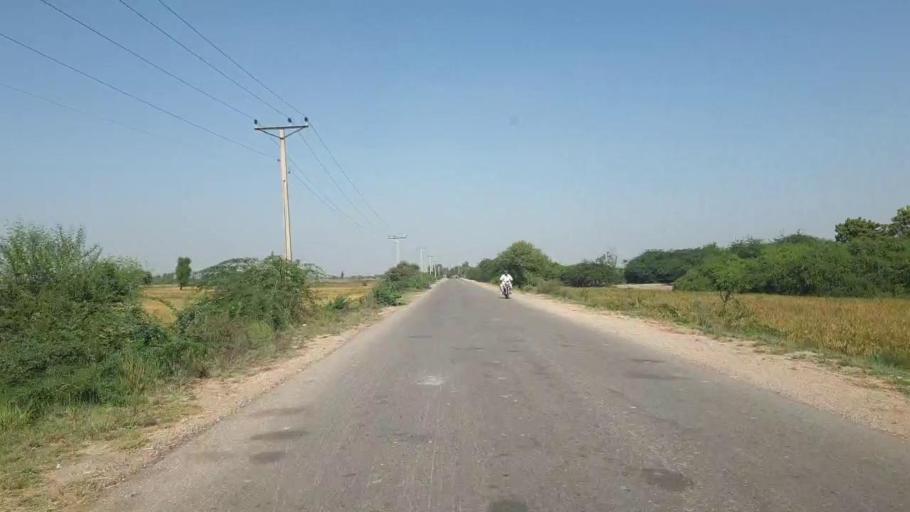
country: PK
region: Sindh
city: Talhar
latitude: 24.9175
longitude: 68.8598
